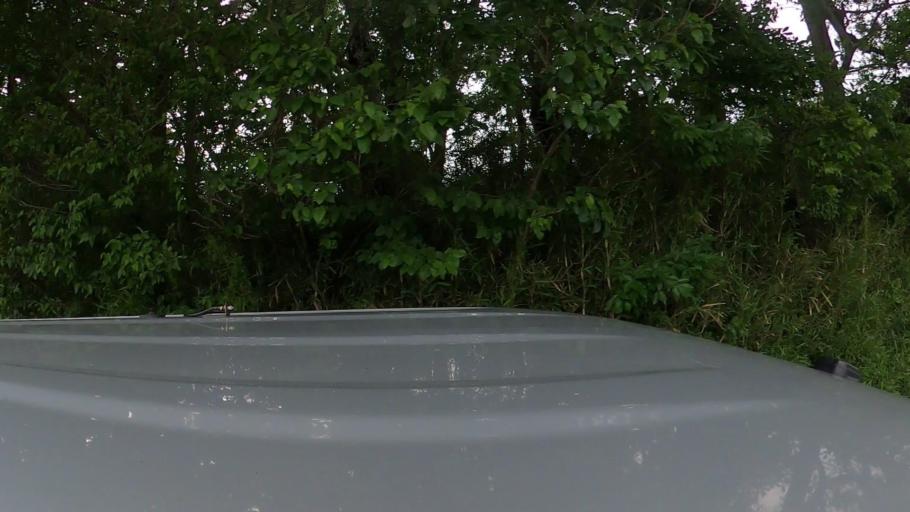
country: JP
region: Ibaraki
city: Ami
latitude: 35.9856
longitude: 140.2488
